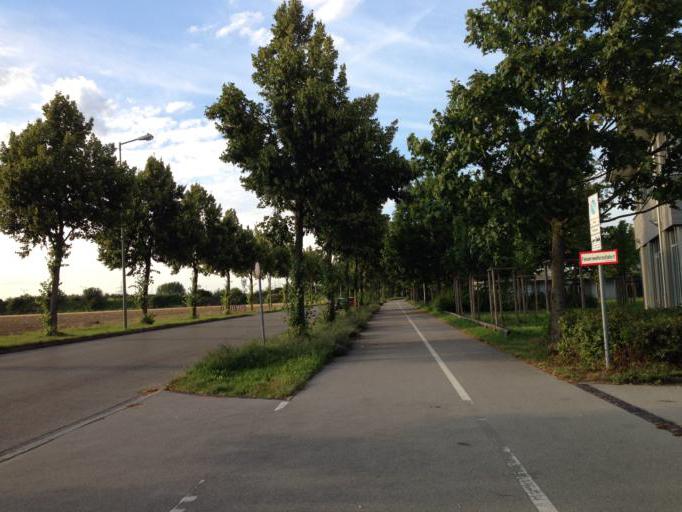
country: DE
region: Bavaria
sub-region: Swabia
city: Augsburg
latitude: 48.3338
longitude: 10.8924
